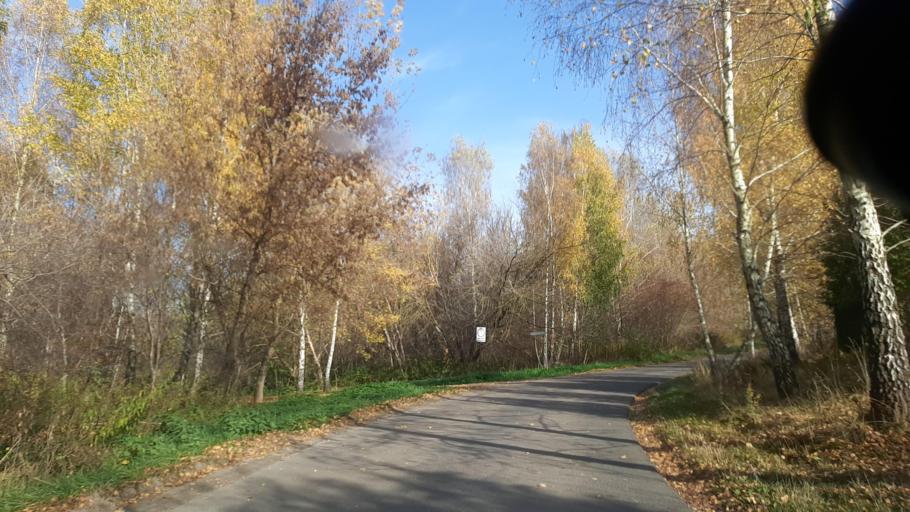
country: PL
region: Lublin Voivodeship
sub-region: Powiat lubelski
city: Lublin
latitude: 51.3182
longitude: 22.5387
